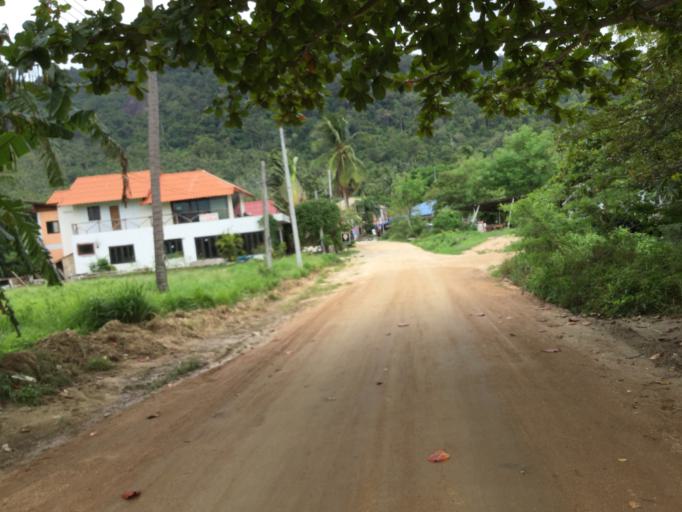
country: TH
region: Nakhon Si Thammarat
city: Ko Pha Ngan
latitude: 9.7701
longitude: 100.0566
